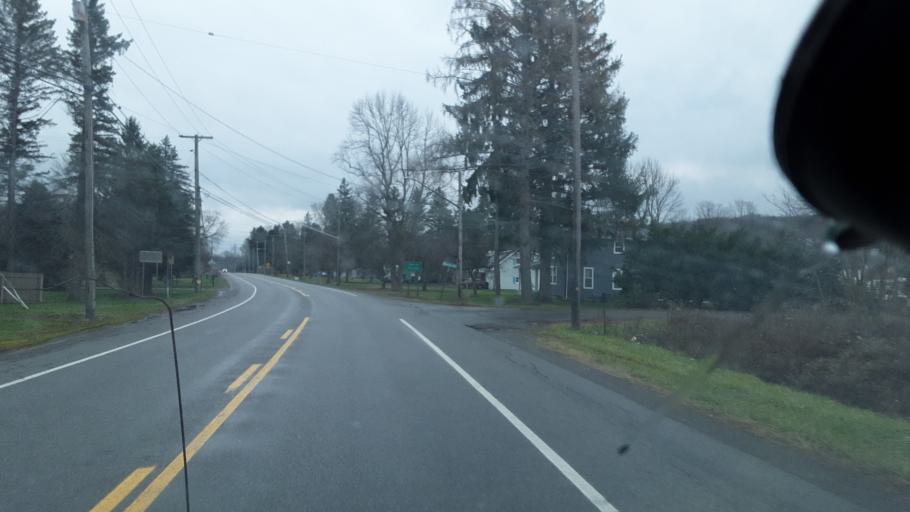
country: US
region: New York
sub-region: Erie County
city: Holland
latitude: 42.6933
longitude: -78.5714
